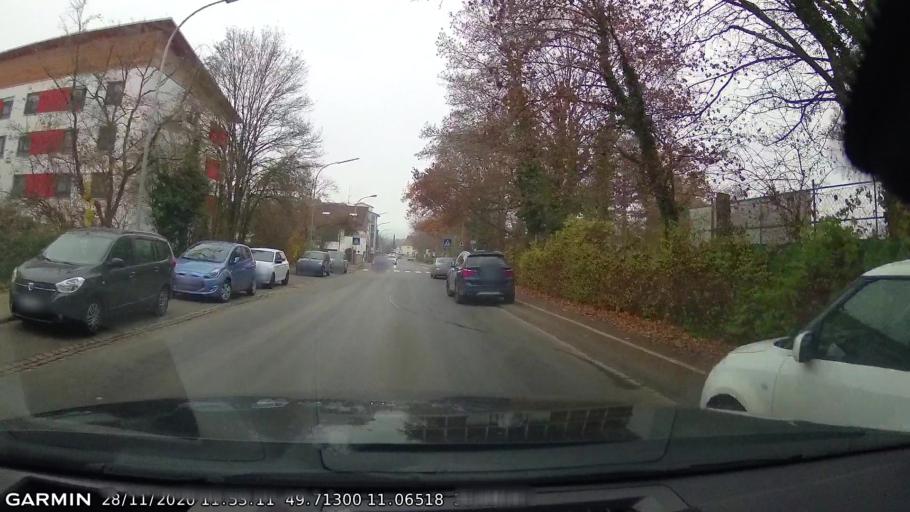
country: DE
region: Bavaria
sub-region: Upper Franconia
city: Forchheim
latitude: 49.7130
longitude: 11.0651
